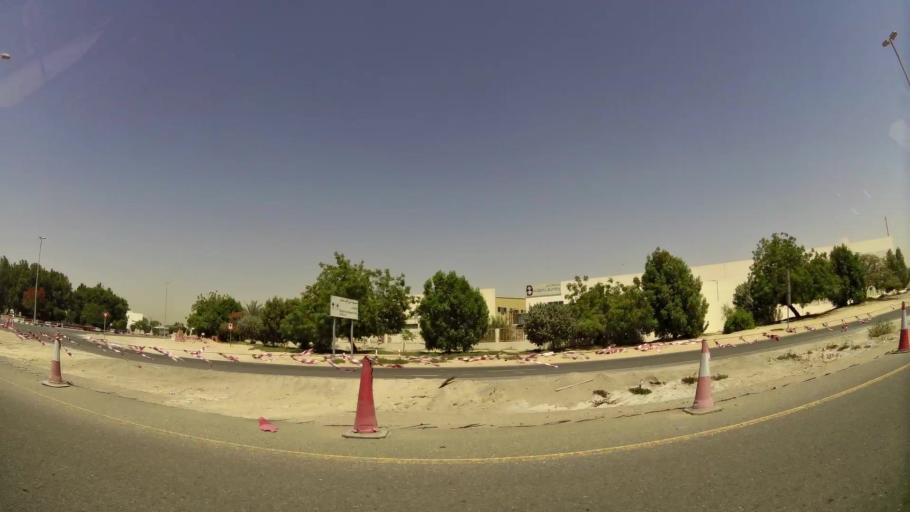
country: AE
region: Dubai
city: Dubai
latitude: 24.9957
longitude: 55.1541
